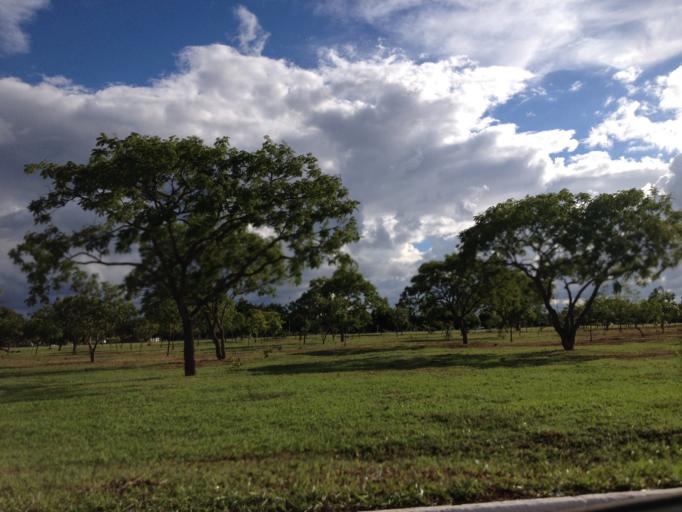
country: BR
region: Federal District
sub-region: Brasilia
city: Brasilia
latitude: -15.7765
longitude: -47.9350
